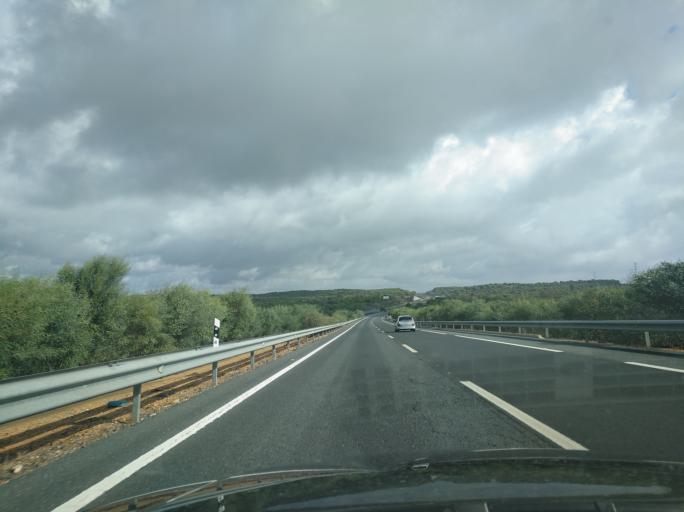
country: ES
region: Andalusia
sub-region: Provincia de Huelva
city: Lepe
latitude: 37.3079
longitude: -7.2009
